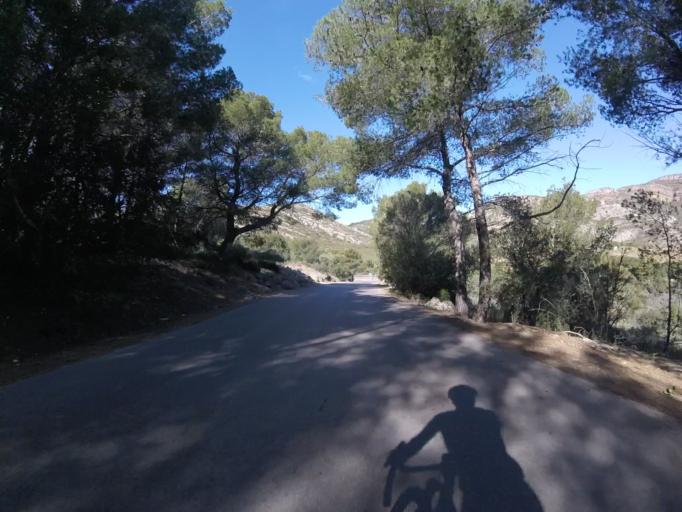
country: ES
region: Valencia
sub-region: Provincia de Castello
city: Orpesa/Oropesa del Mar
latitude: 40.0738
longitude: 0.1122
